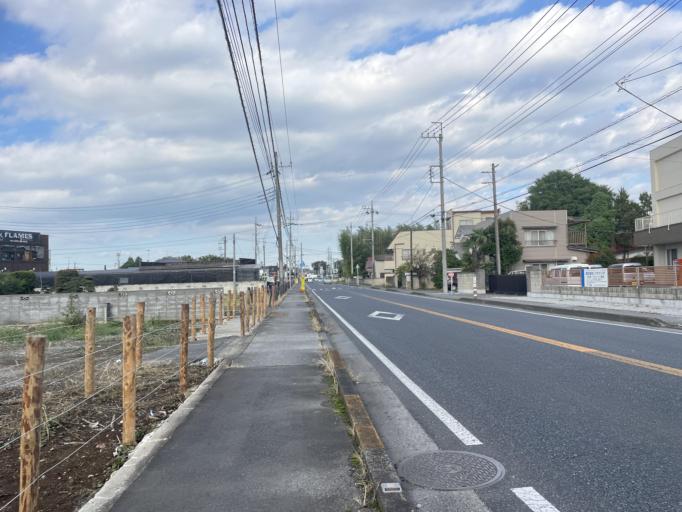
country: JP
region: Tochigi
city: Oyama
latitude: 36.2825
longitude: 139.7775
